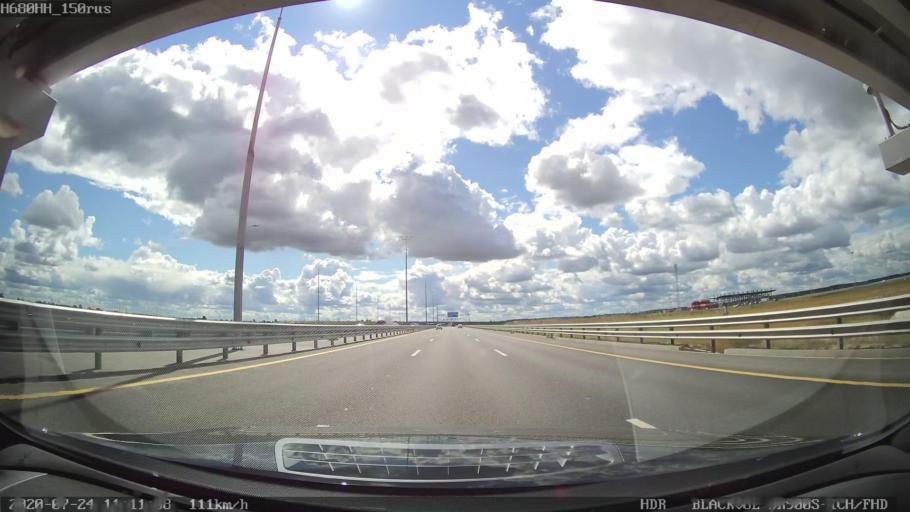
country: RU
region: St.-Petersburg
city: Tyarlevo
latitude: 59.7275
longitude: 30.5113
